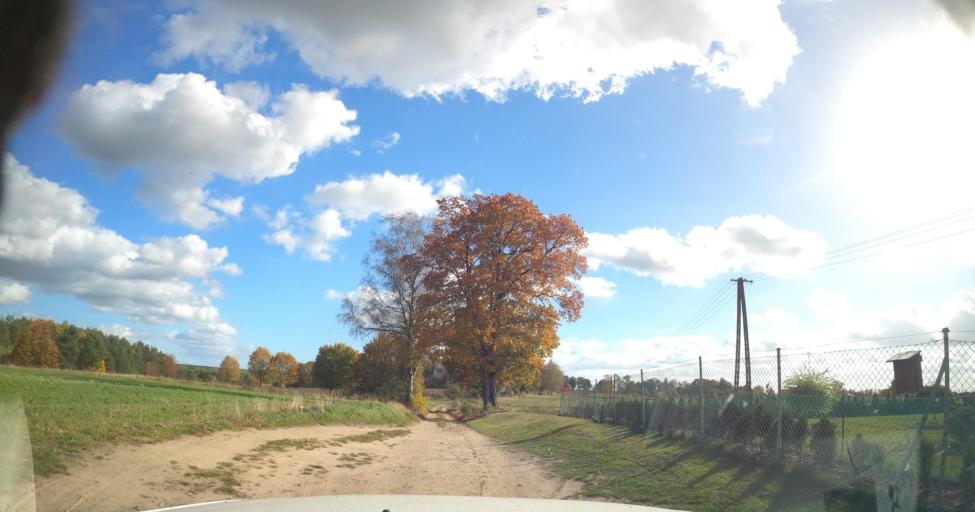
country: PL
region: West Pomeranian Voivodeship
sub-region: Powiat szczecinecki
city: Lubowo
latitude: 53.5868
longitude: 16.4416
